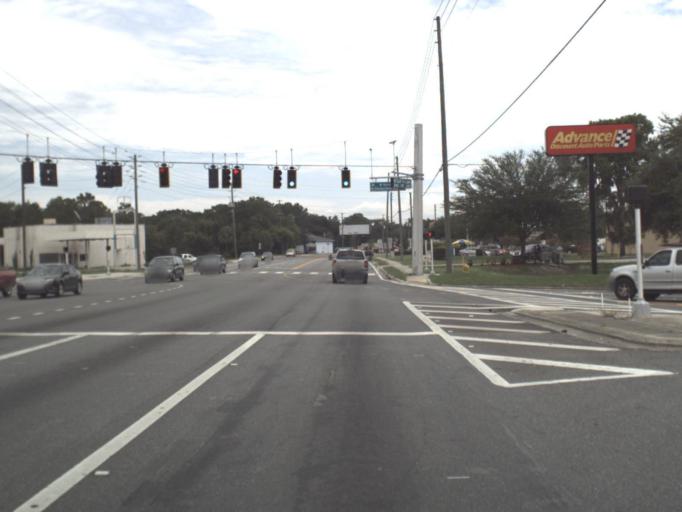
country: US
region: Florida
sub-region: Citrus County
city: Crystal River
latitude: 28.8917
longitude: -82.5493
